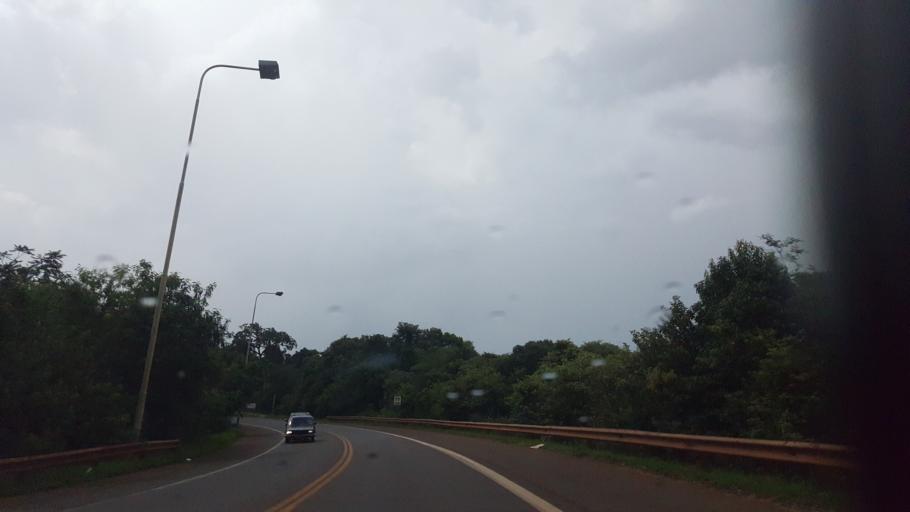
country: AR
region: Misiones
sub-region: Departamento de Iguazu
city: Puerto Iguazu
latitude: -25.6103
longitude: -54.5607
